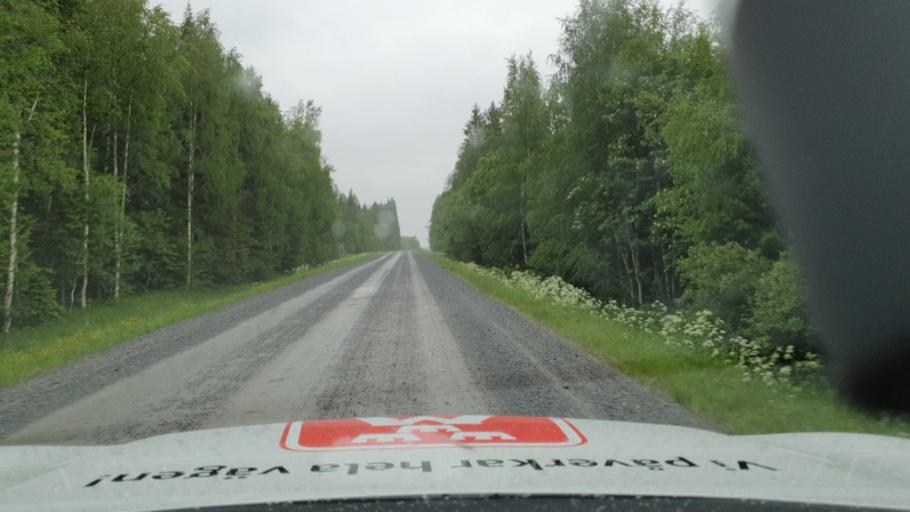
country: SE
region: Vaesterbotten
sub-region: Nordmalings Kommun
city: Nordmaling
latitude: 63.8276
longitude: 19.4897
